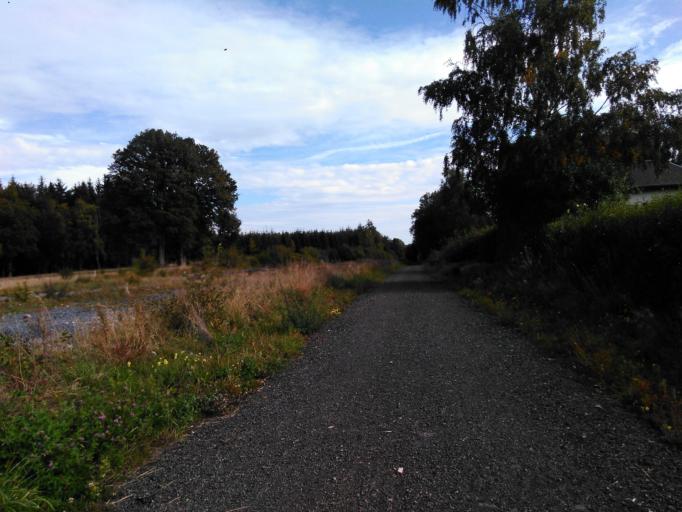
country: BE
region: Wallonia
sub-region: Province du Luxembourg
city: Vaux-sur-Sure
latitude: 49.9480
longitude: 5.6006
